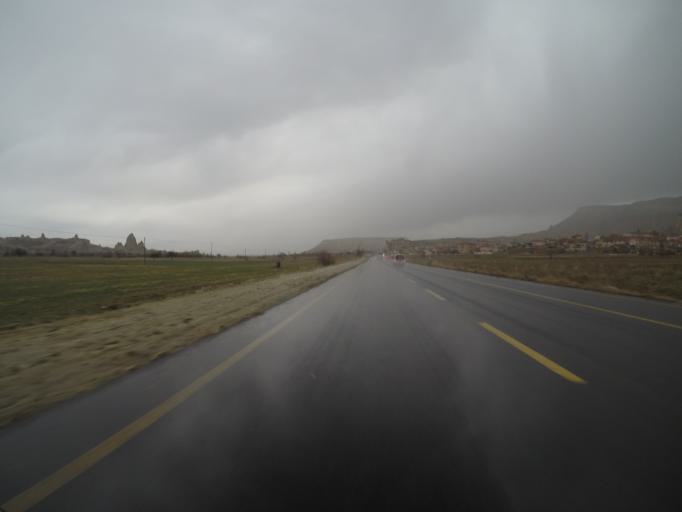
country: TR
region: Nevsehir
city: Goereme
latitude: 38.6676
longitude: 34.8346
